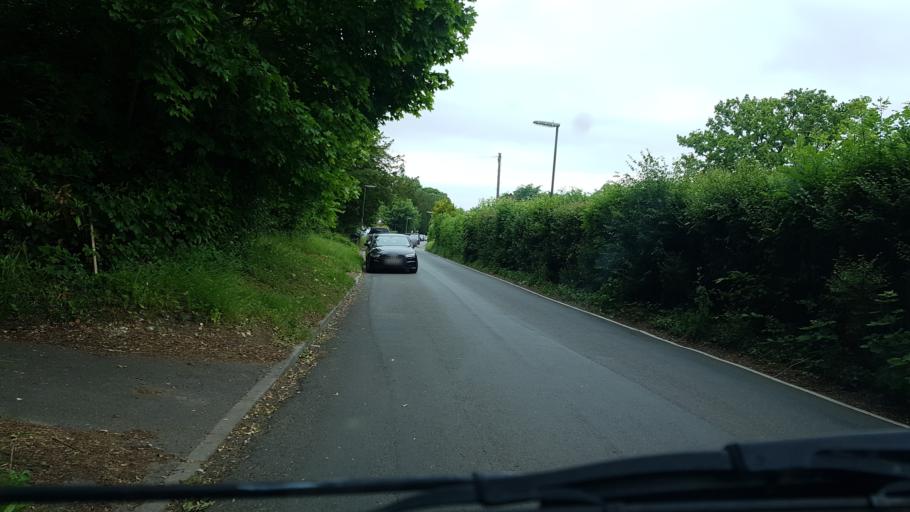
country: GB
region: England
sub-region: Surrey
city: Great Bookham
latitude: 51.2757
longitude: -0.3702
